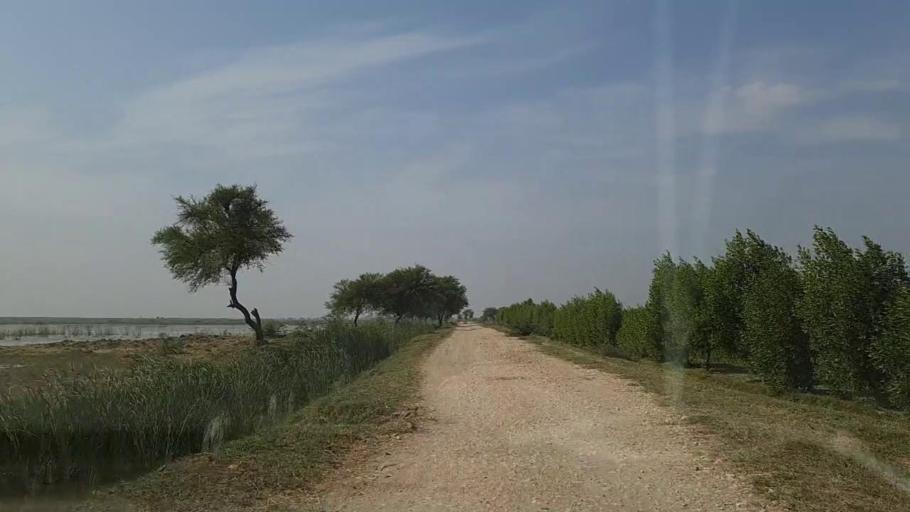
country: PK
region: Sindh
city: Mirpur Batoro
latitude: 24.6110
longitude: 68.2263
